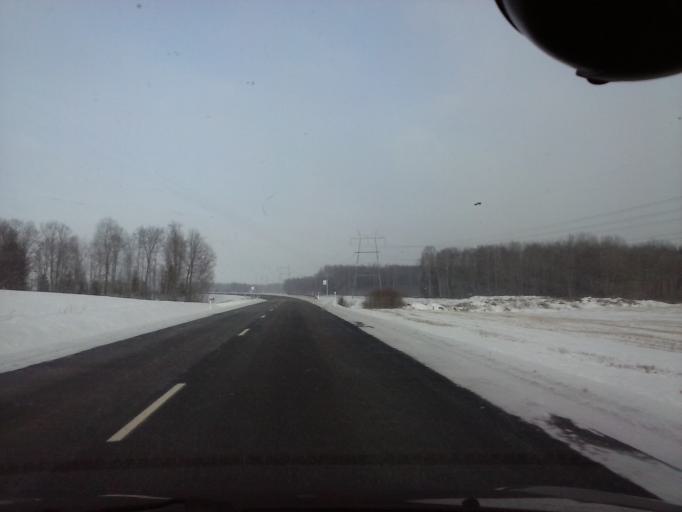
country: EE
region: Viljandimaa
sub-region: Abja vald
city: Abja-Paluoja
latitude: 58.2888
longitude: 25.2937
